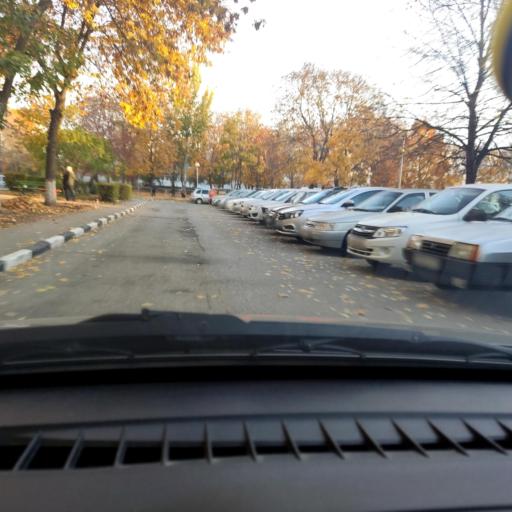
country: RU
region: Samara
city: Tol'yatti
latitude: 53.5355
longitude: 49.3216
